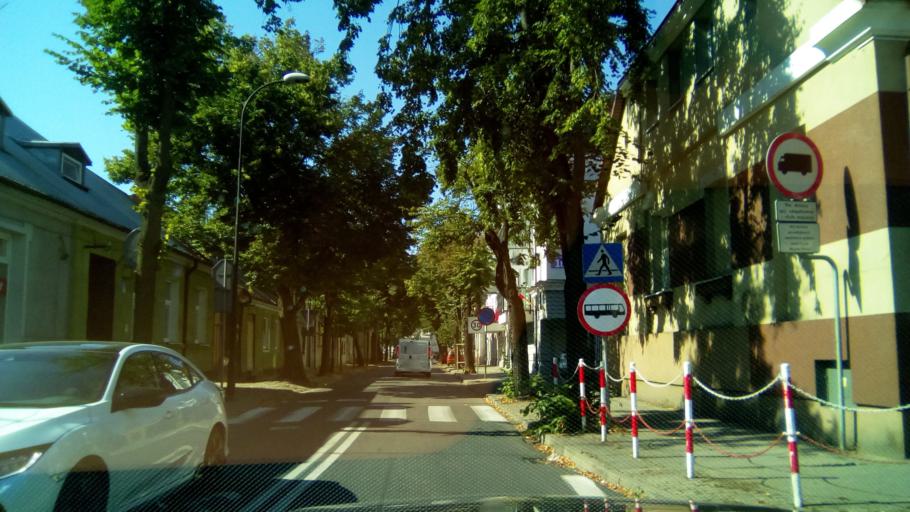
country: PL
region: Masovian Voivodeship
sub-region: Plock
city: Plock
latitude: 52.5421
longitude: 19.6971
